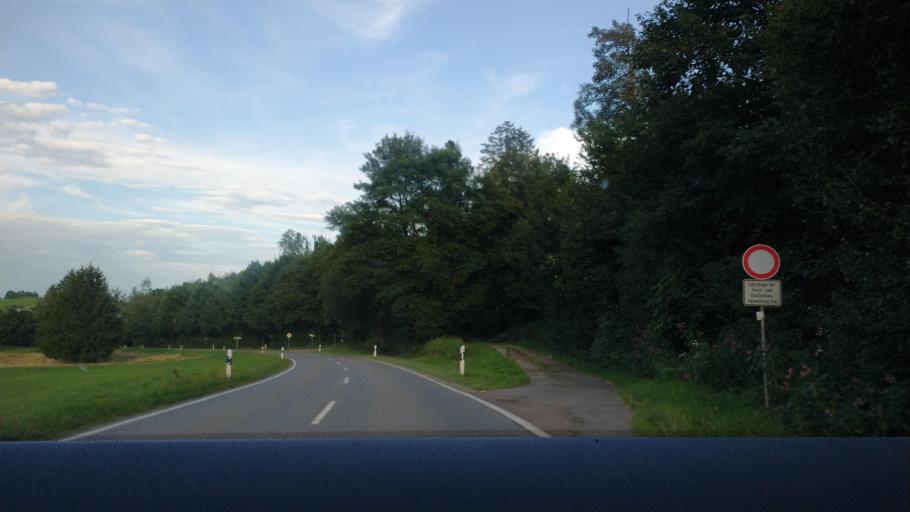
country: DE
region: Bavaria
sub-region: Swabia
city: Hergensweiler
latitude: 47.6306
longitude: 9.7461
